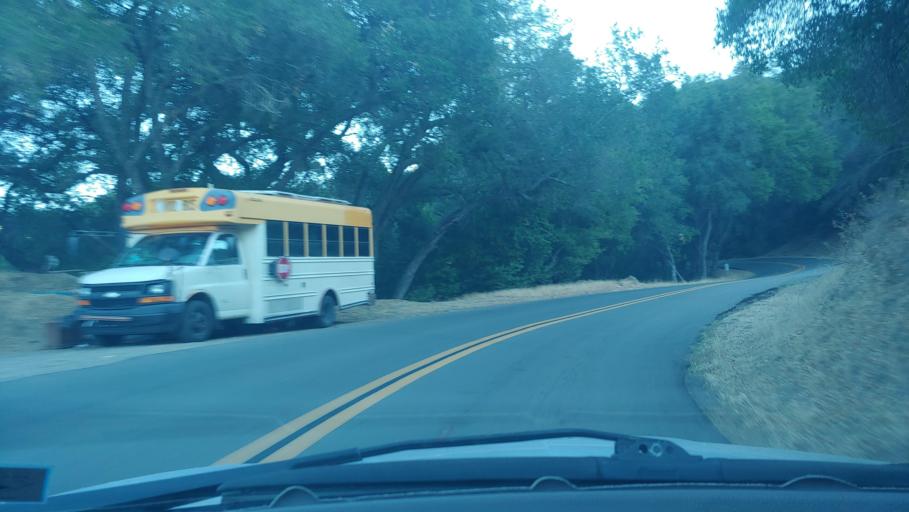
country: US
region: California
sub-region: Santa Barbara County
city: Goleta
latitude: 34.5334
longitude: -119.8412
